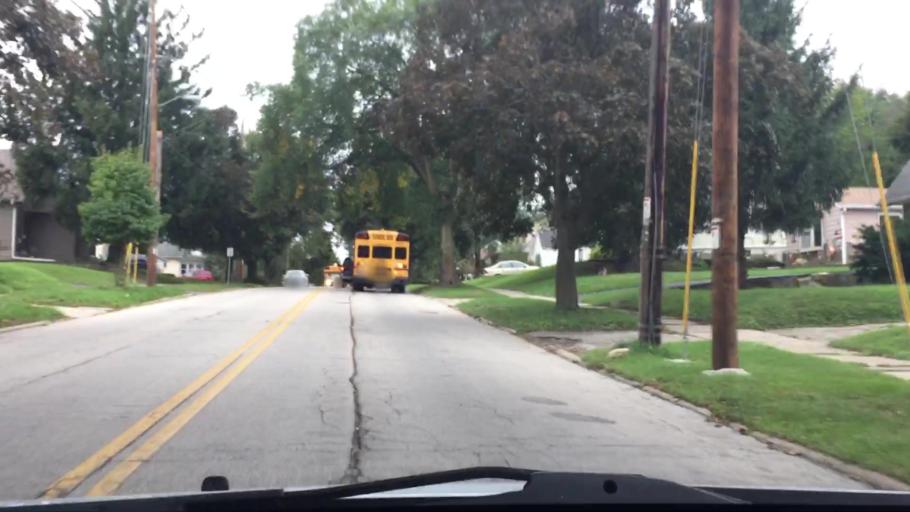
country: US
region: Wisconsin
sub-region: Waukesha County
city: Waukesha
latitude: 43.0155
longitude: -88.2128
